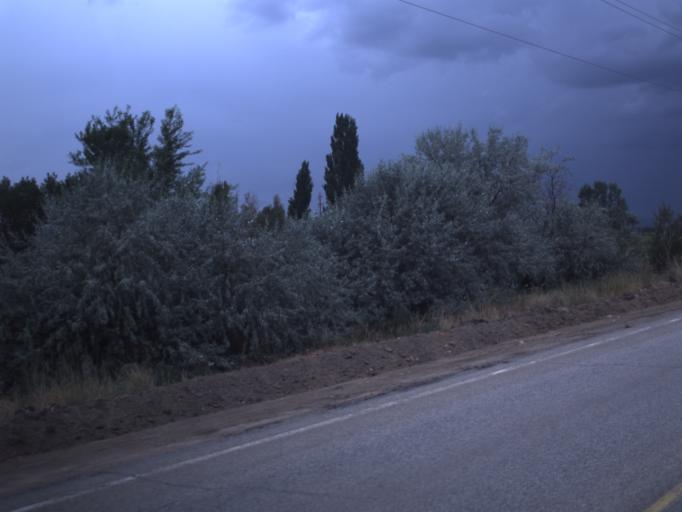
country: US
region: Utah
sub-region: Duchesne County
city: Roosevelt
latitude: 40.3343
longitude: -110.0219
